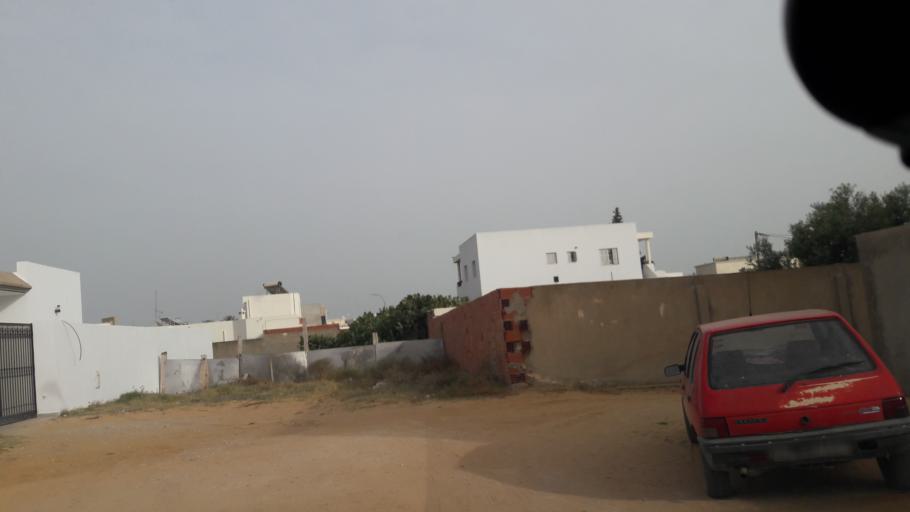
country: TN
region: Safaqis
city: Al Qarmadah
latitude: 34.7801
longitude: 10.7734
